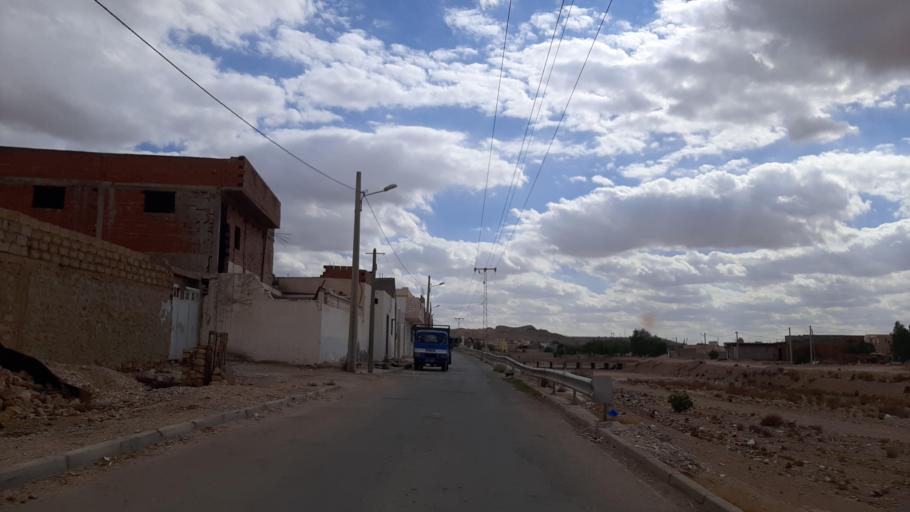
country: TN
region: Tataouine
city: Tataouine
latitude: 32.9400
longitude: 10.4514
